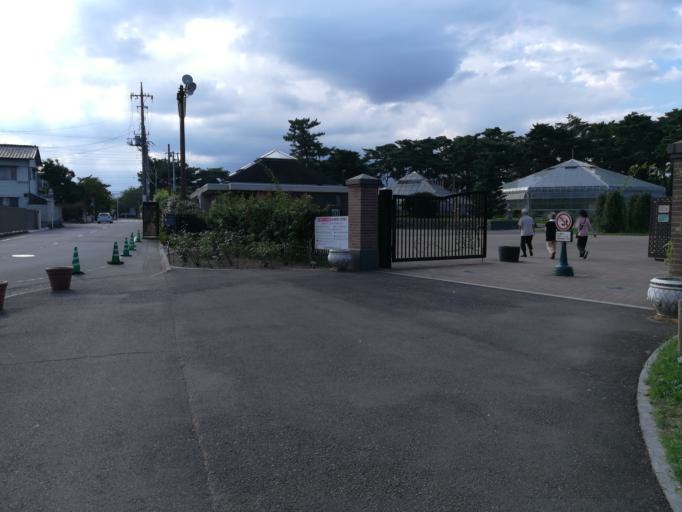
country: JP
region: Gunma
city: Maebashi-shi
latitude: 36.4182
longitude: 139.0496
